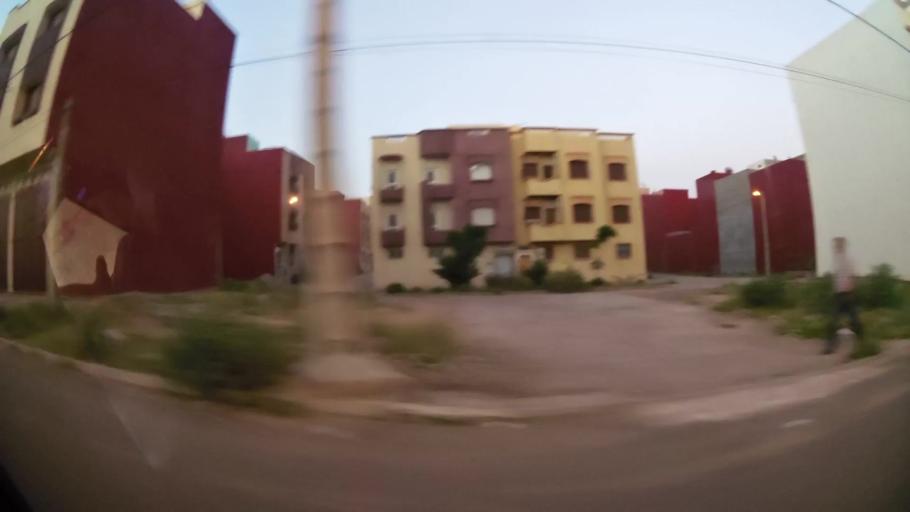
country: MA
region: Souss-Massa-Draa
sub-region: Inezgane-Ait Mellou
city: Inezgane
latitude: 30.3794
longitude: -9.4822
